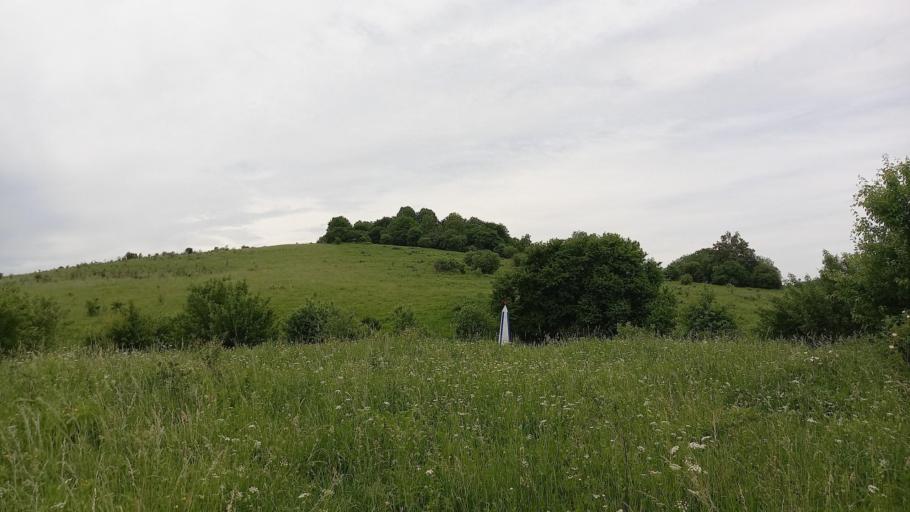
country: RU
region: Karachayevo-Cherkesiya
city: Pregradnaya
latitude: 44.0998
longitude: 41.1924
